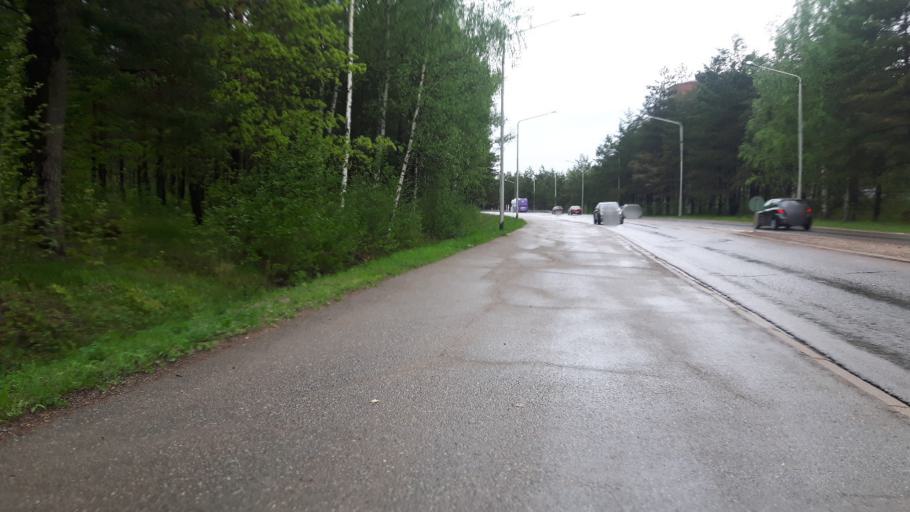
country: FI
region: Kymenlaakso
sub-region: Kotka-Hamina
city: Kotka
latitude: 60.4882
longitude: 26.9041
